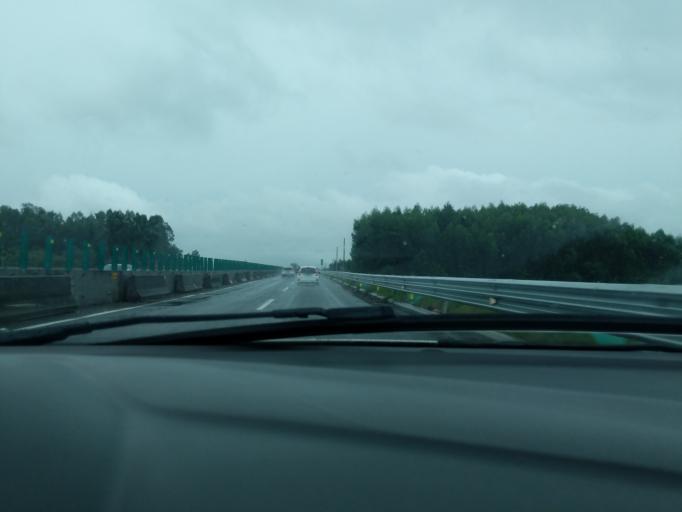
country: CN
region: Guangdong
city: Yueshan
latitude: 22.4631
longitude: 112.7368
